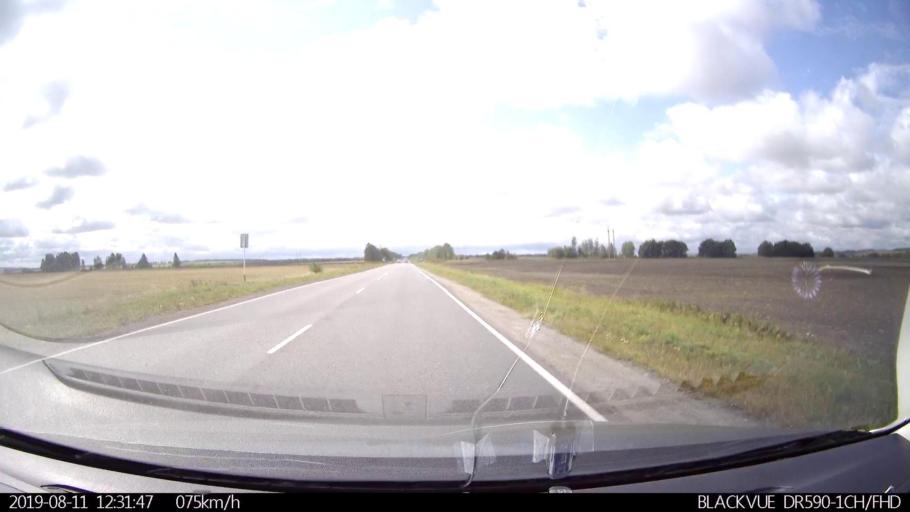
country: RU
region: Ulyanovsk
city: Ignatovka
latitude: 53.8174
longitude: 47.8799
